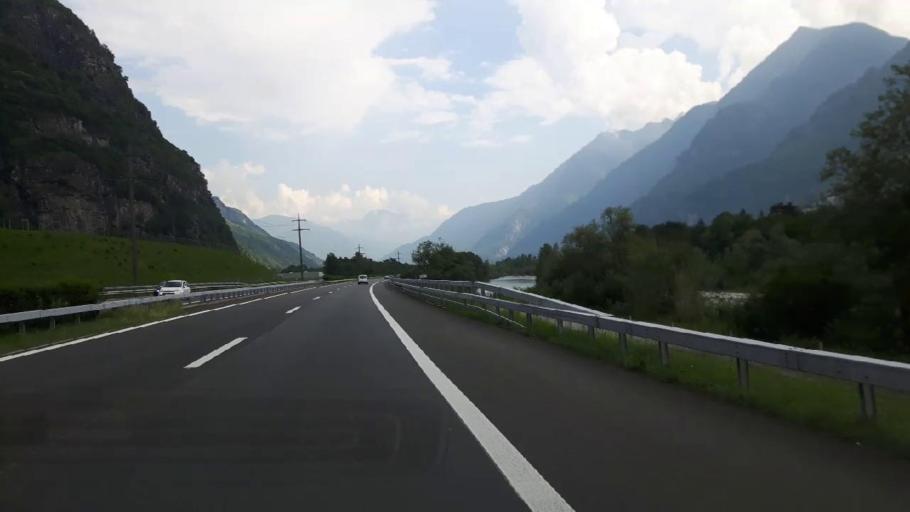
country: CH
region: Ticino
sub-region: Riviera District
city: Lodrino
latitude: 46.3266
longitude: 8.9792
